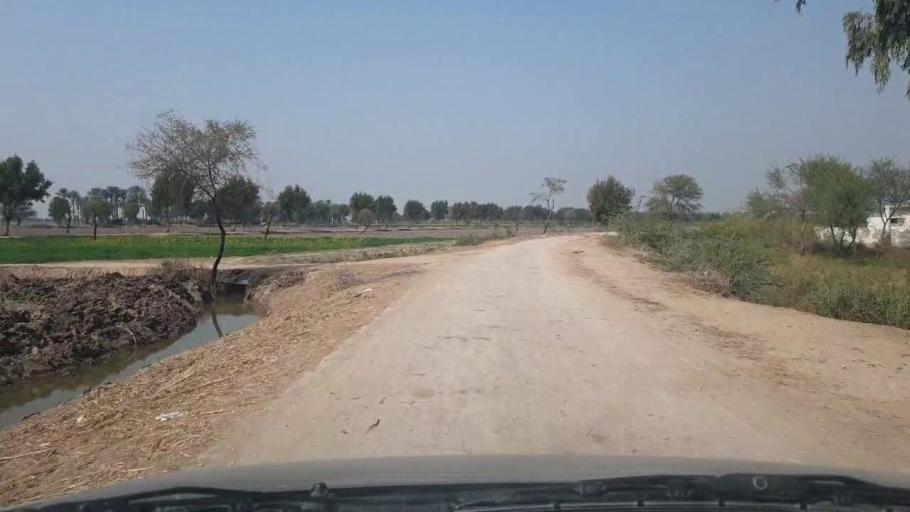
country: PK
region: Sindh
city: Mirwah Gorchani
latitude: 25.3584
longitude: 69.1443
